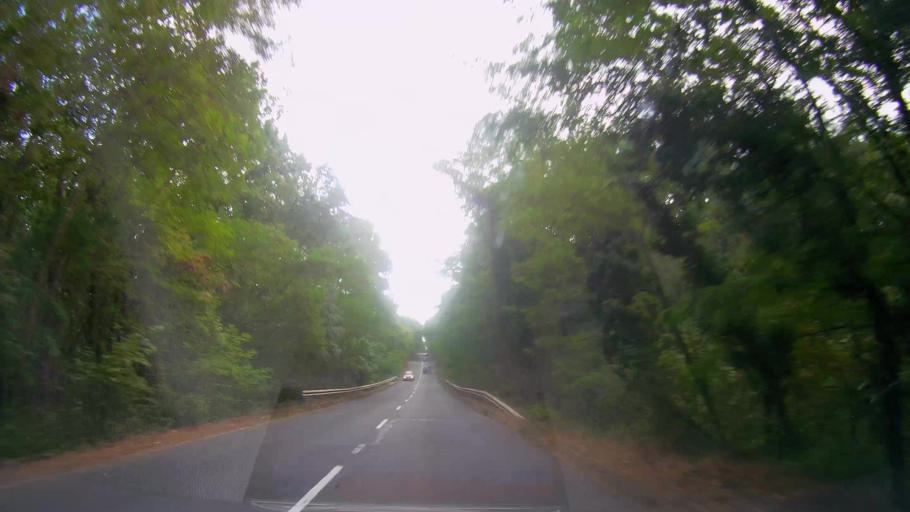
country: BG
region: Burgas
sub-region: Obshtina Primorsko
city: Primorsko
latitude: 42.2868
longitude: 27.7360
